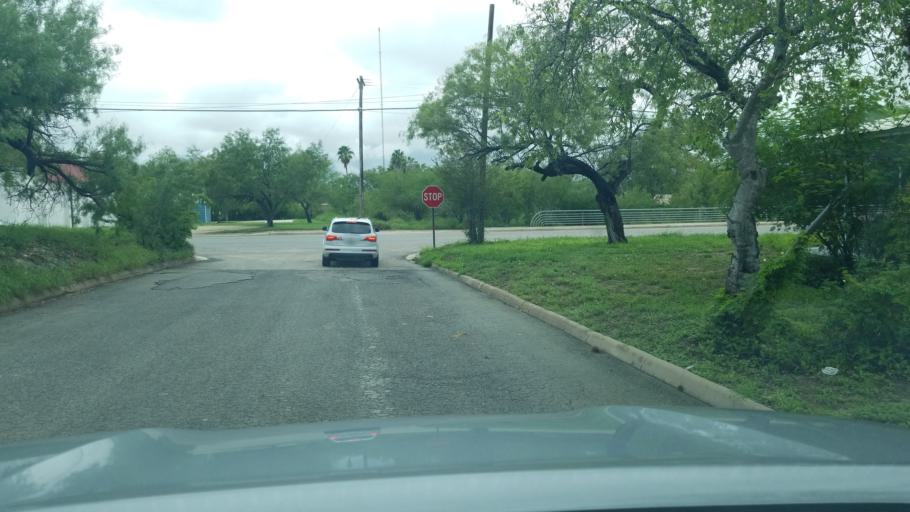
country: US
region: Texas
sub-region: Dimmit County
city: Carrizo Springs
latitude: 28.5212
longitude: -99.8612
